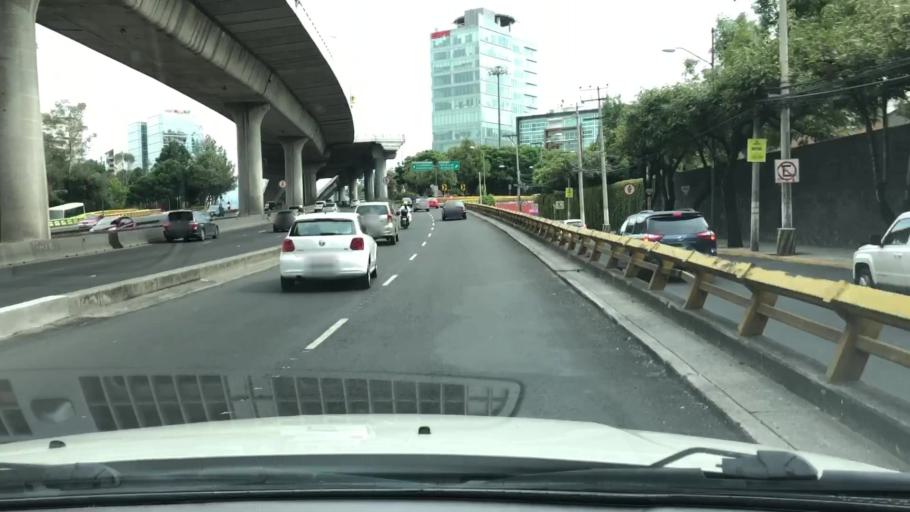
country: MX
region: Mexico City
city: Magdalena Contreras
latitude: 19.3131
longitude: -99.2206
